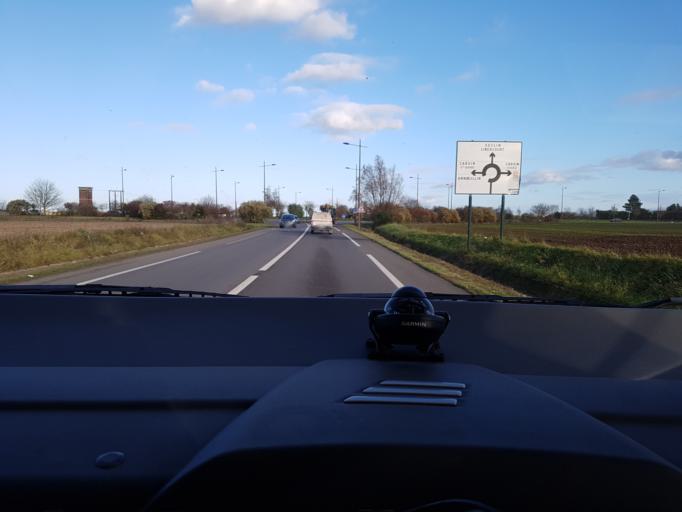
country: FR
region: Nord-Pas-de-Calais
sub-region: Departement du Pas-de-Calais
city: Carvin
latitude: 50.5045
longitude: 2.9485
